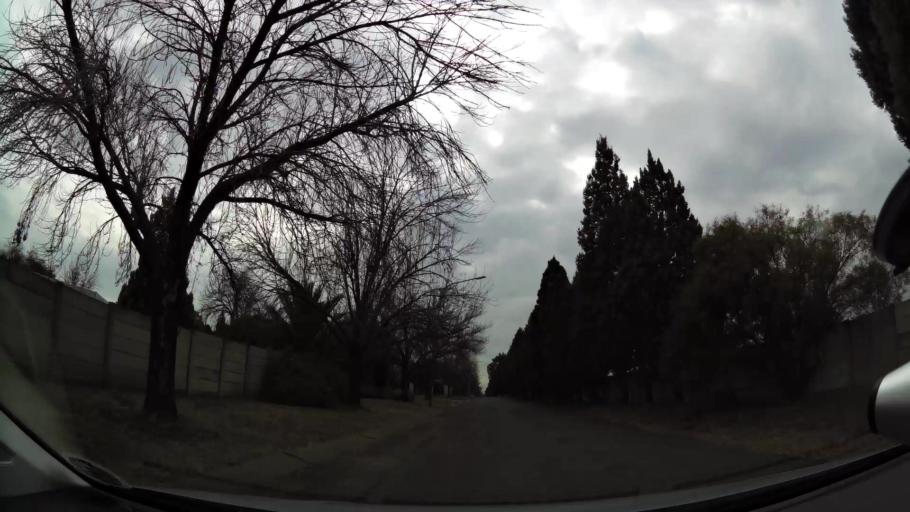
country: ZA
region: Orange Free State
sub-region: Fezile Dabi District Municipality
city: Kroonstad
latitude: -27.6803
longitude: 27.2475
